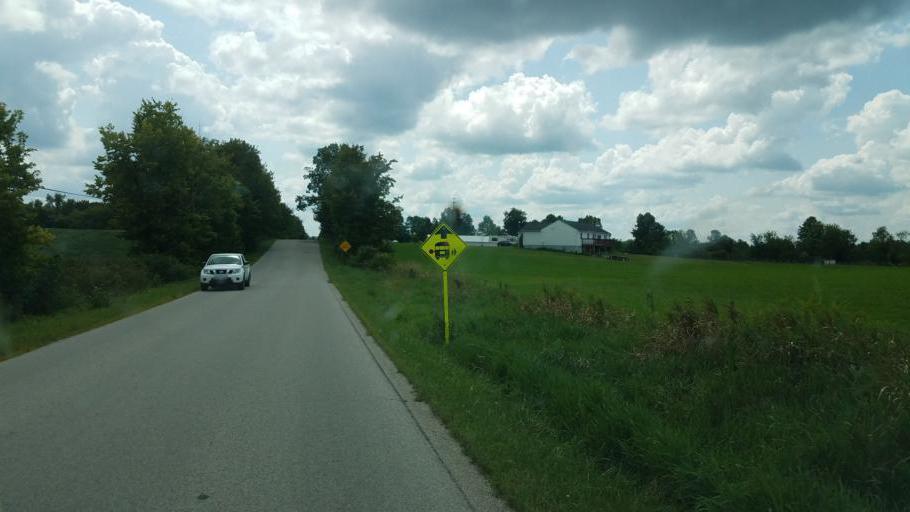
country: US
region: Ohio
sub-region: Morrow County
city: Cardington
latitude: 40.4308
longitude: -82.8088
